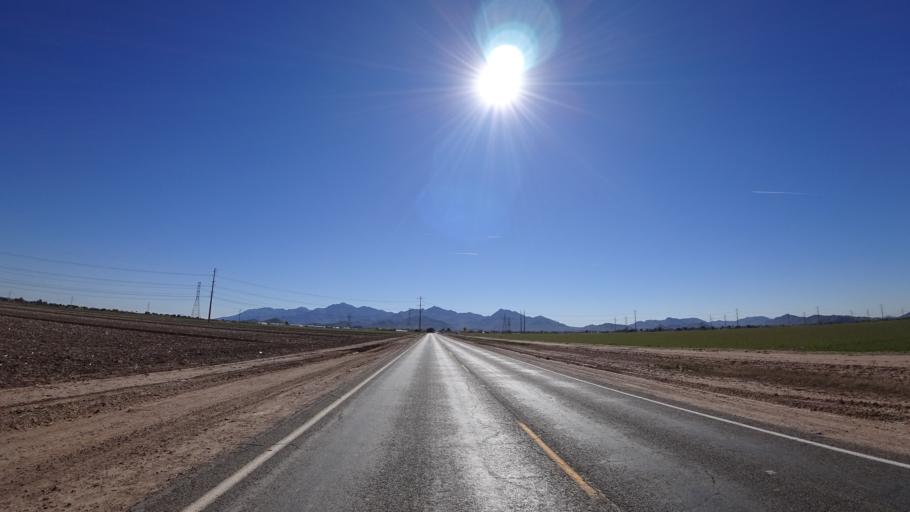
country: US
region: Arizona
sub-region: Maricopa County
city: Avondale
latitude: 33.4086
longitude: -112.3234
